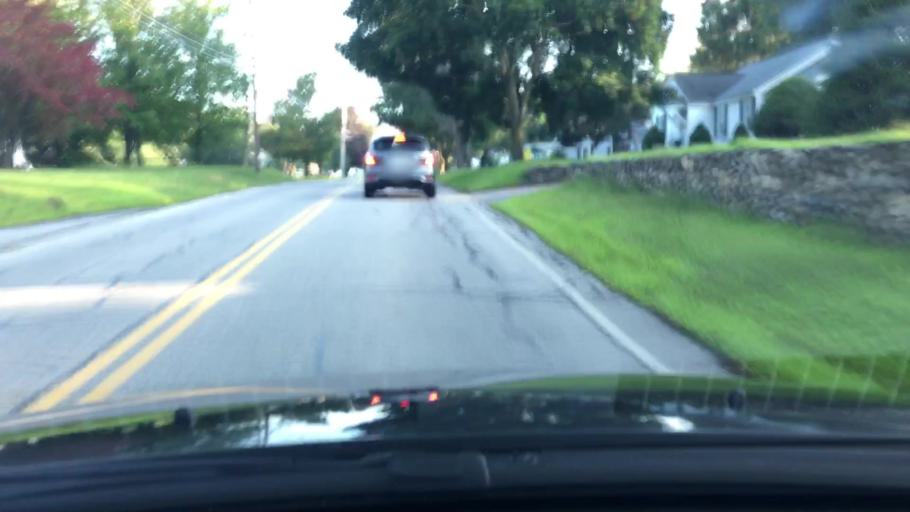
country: US
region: Massachusetts
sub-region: Worcester County
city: West Boylston
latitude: 42.3497
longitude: -71.7790
